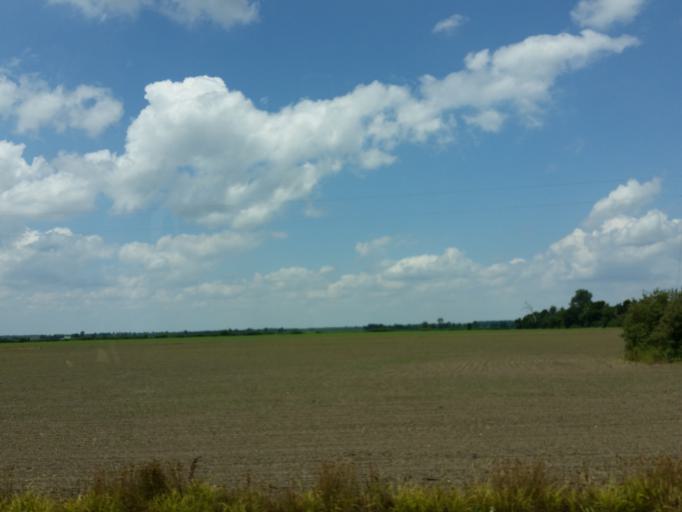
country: US
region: Kentucky
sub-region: Fulton County
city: Hickman
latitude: 36.5384
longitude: -89.3387
